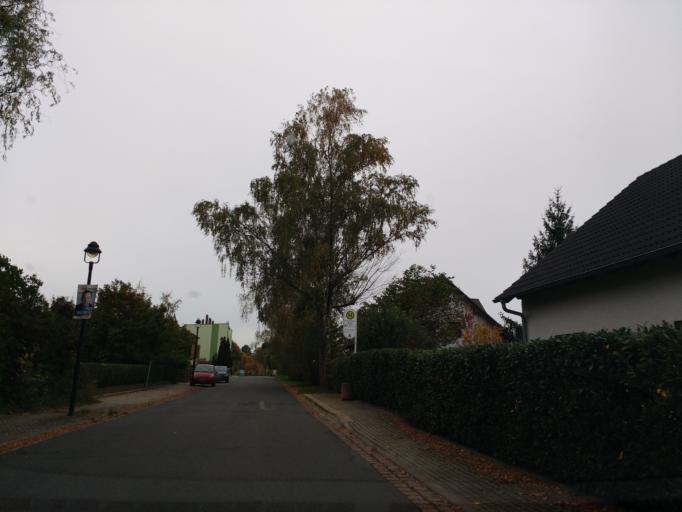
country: DE
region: Saxony-Anhalt
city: Gutenberg
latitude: 51.5273
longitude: 11.9711
